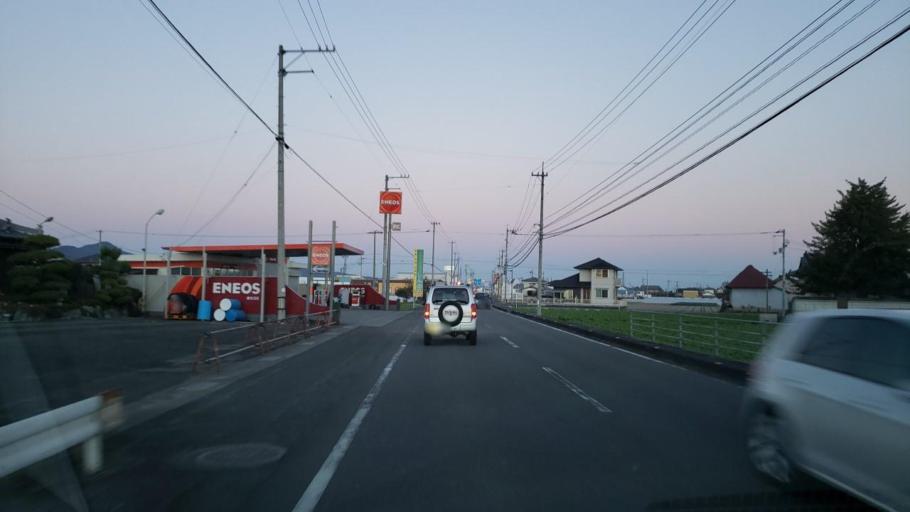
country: JP
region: Tokushima
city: Ishii
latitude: 34.1181
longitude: 134.4284
